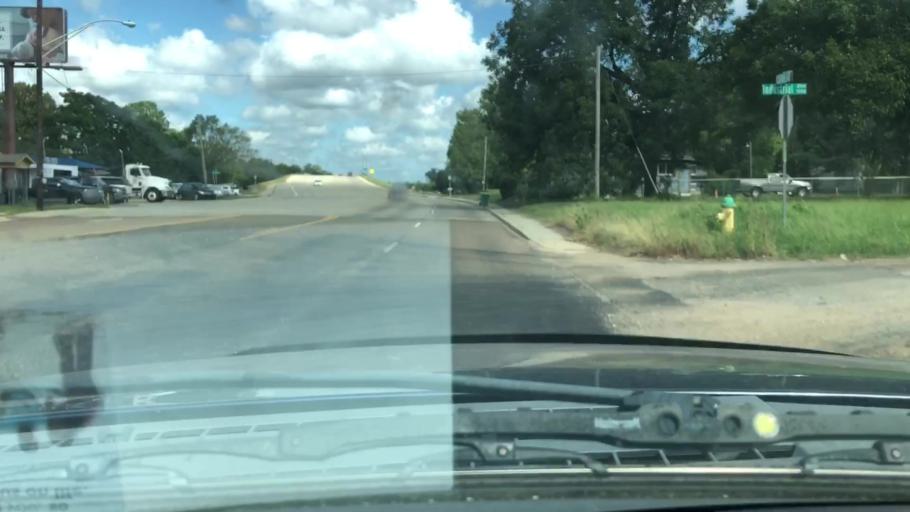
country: US
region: Texas
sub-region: Bowie County
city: Texarkana
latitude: 33.4100
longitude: -94.0605
